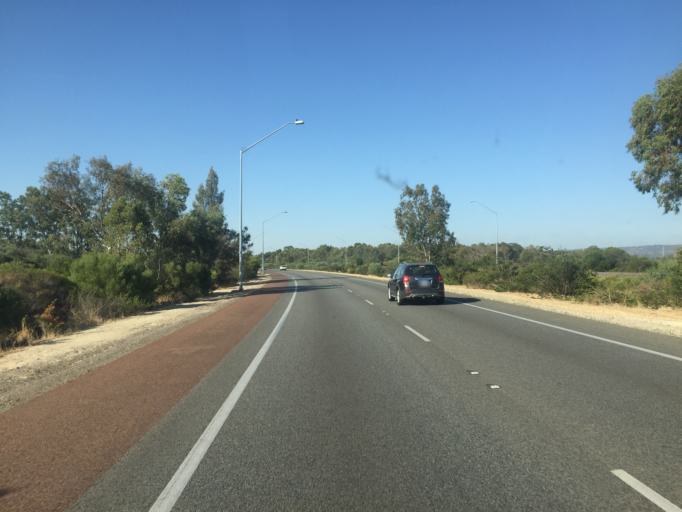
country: AU
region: Western Australia
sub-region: Gosnells
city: Kenwick
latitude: -32.0260
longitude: 115.9711
